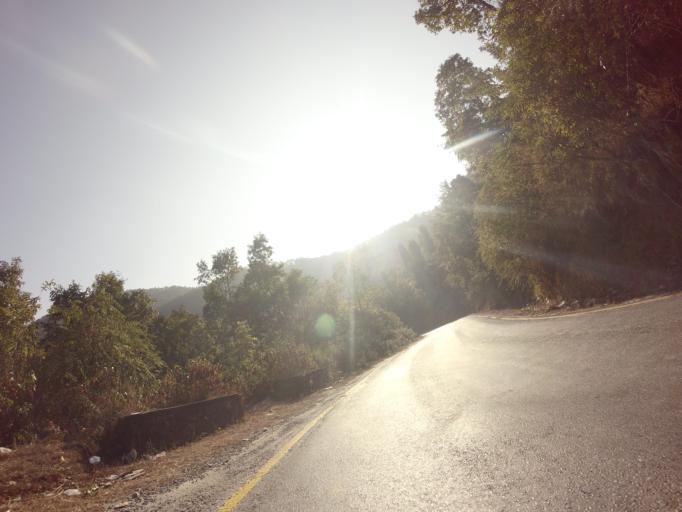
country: NP
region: Western Region
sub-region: Gandaki Zone
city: Pokhara
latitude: 28.1896
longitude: 83.9008
